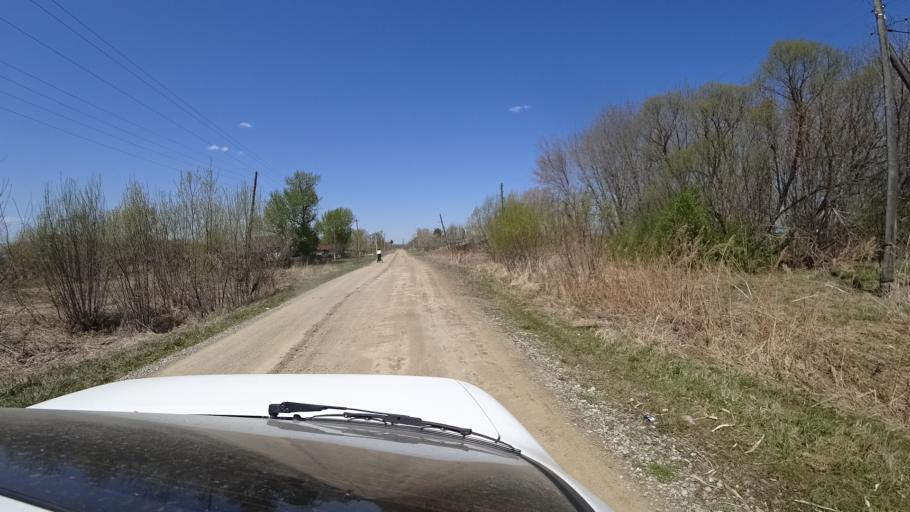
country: RU
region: Primorskiy
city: Lazo
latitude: 45.7971
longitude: 133.7647
